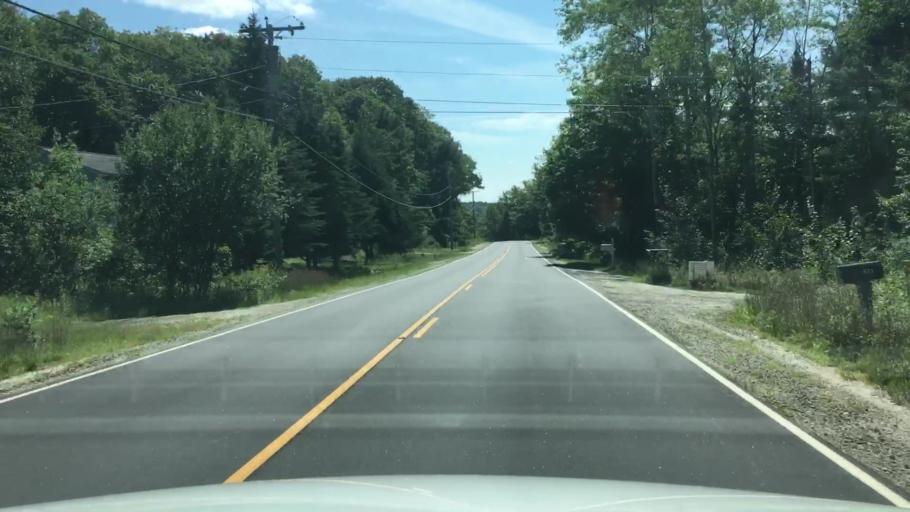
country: US
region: Maine
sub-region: Sagadahoc County
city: Topsham
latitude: 43.9829
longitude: -69.9859
